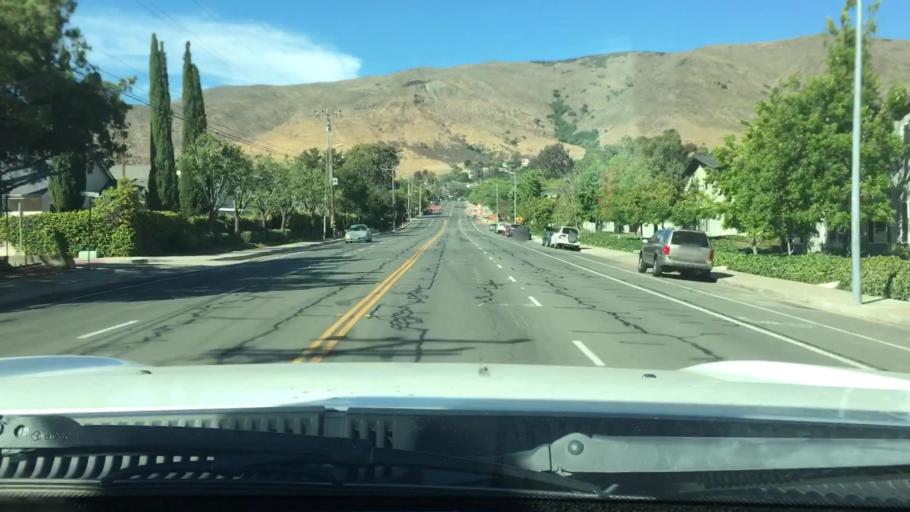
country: US
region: California
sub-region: San Luis Obispo County
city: San Luis Obispo
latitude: 35.2633
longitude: -120.6421
